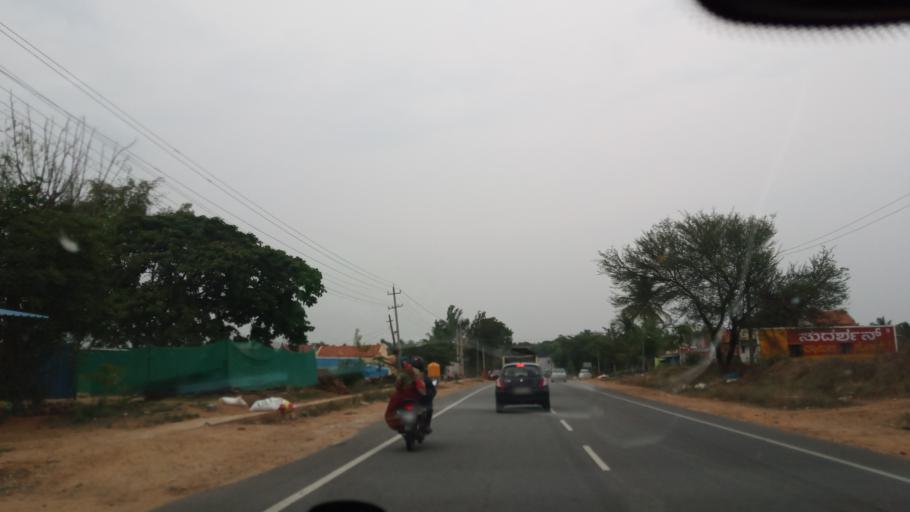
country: IN
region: Karnataka
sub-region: Mandya
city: Belluru
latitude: 12.9372
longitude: 76.7504
